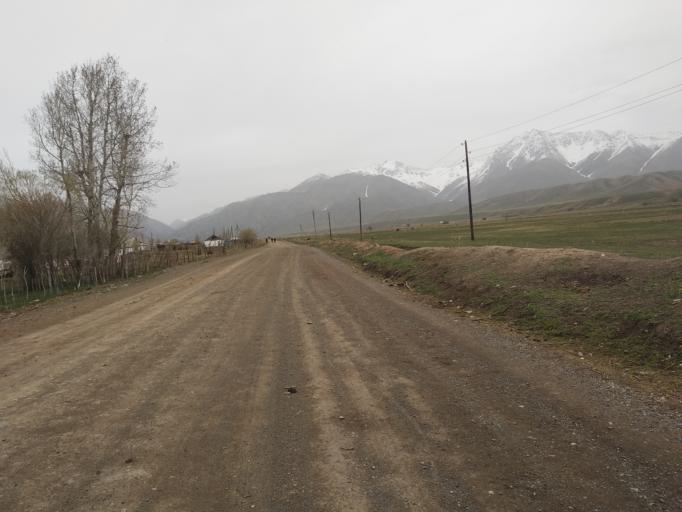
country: KG
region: Naryn
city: Naryn
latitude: 41.5171
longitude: 76.4406
